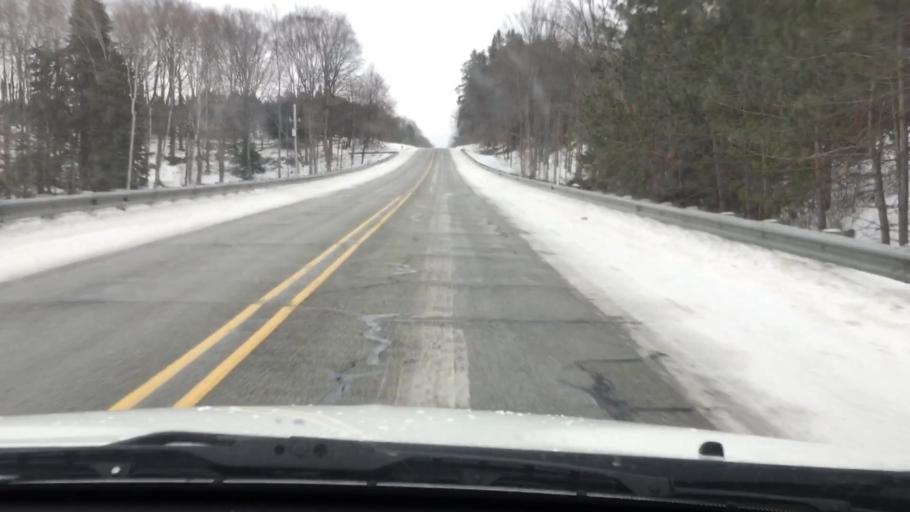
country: US
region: Michigan
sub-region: Wexford County
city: Cadillac
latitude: 44.1773
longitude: -85.4055
